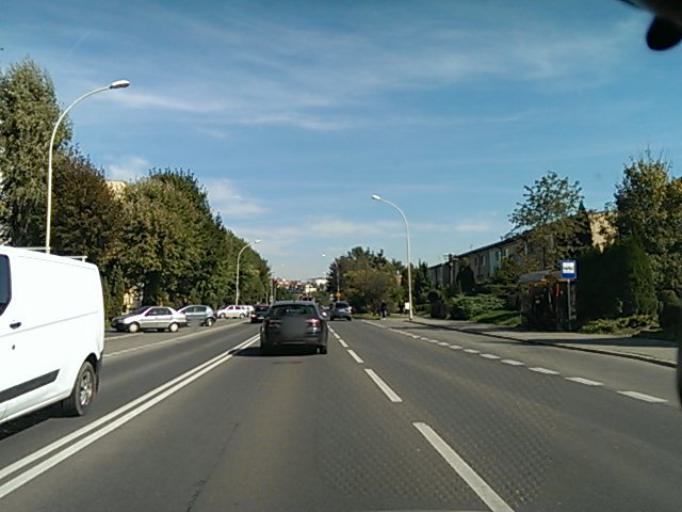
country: PL
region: Subcarpathian Voivodeship
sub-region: Rzeszow
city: Rzeszow
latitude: 50.0300
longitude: 22.0234
